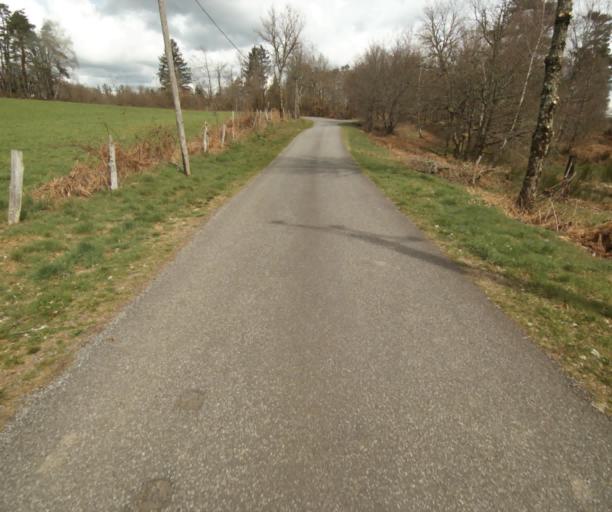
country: FR
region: Limousin
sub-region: Departement de la Correze
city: Correze
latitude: 45.3460
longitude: 1.9387
